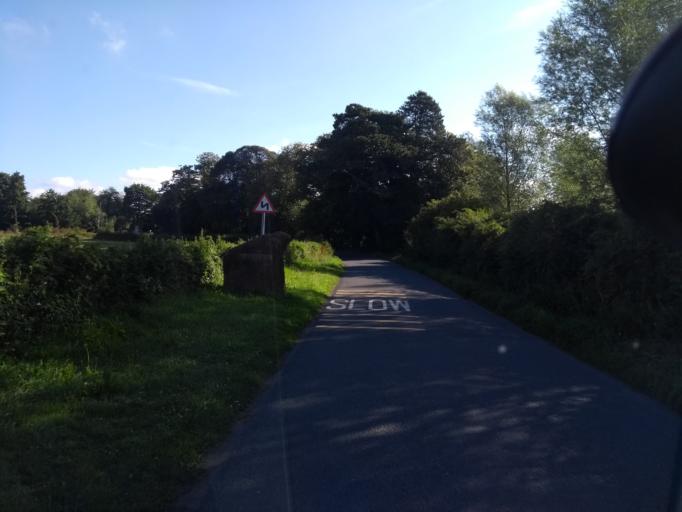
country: GB
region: England
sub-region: Somerset
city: South Petherton
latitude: 50.9635
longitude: -2.7919
